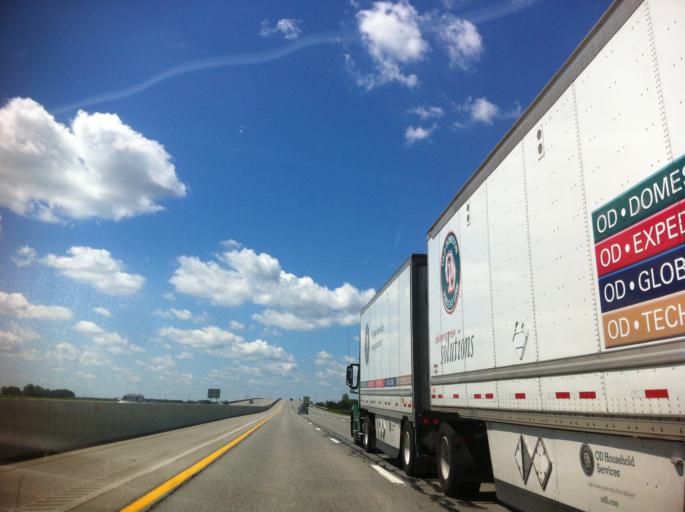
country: US
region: Ohio
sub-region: Wood County
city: Walbridge
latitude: 41.5387
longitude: -83.5008
